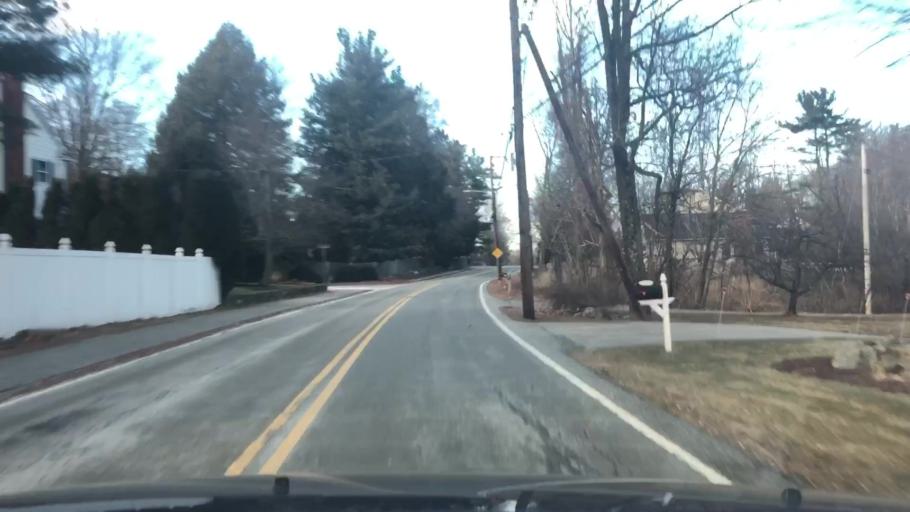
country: US
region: Massachusetts
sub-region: Essex County
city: Andover
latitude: 42.6742
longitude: -71.1142
